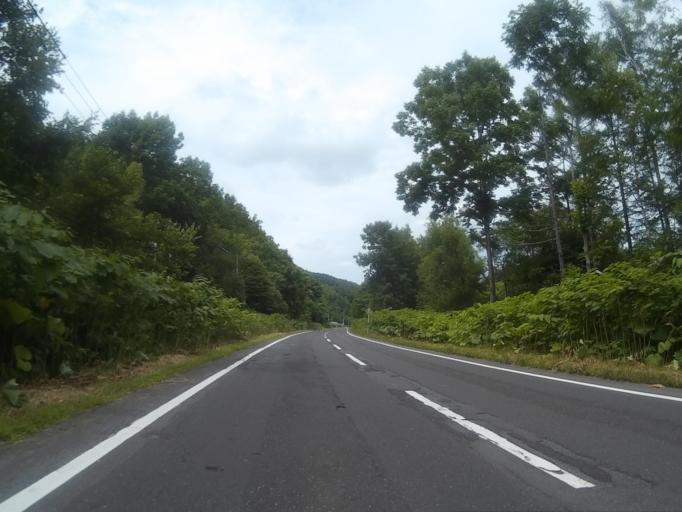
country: JP
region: Hokkaido
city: Niseko Town
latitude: 42.8188
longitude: 141.0022
